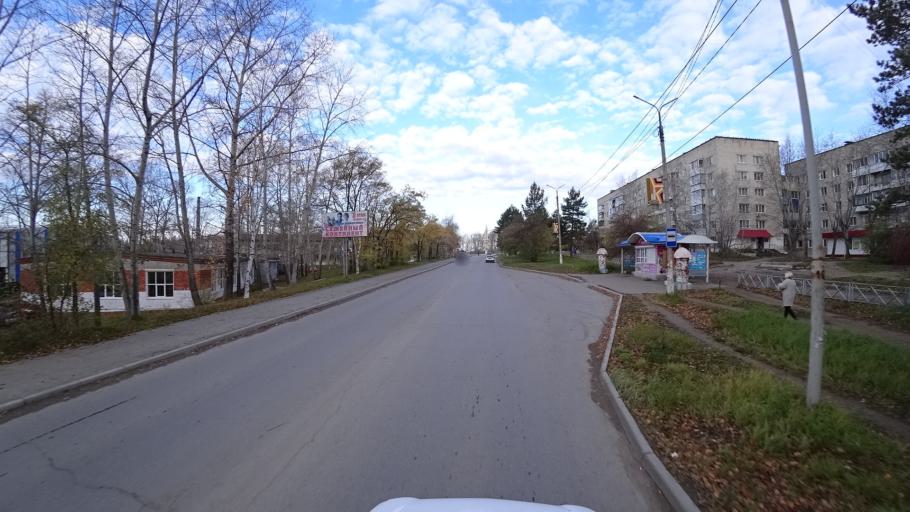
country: RU
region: Khabarovsk Krai
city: Amursk
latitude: 50.2289
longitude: 136.9045
